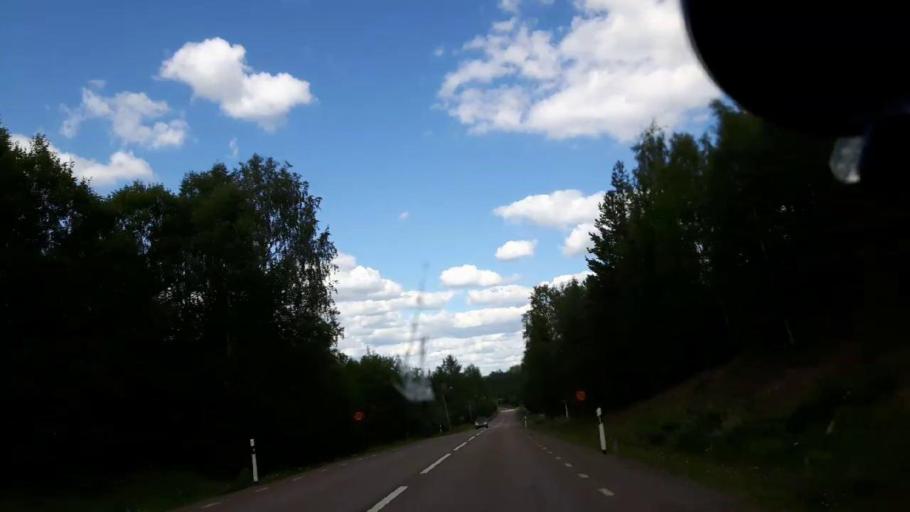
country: SE
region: Jaemtland
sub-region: Ragunda Kommun
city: Hammarstrand
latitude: 62.9930
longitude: 16.6771
